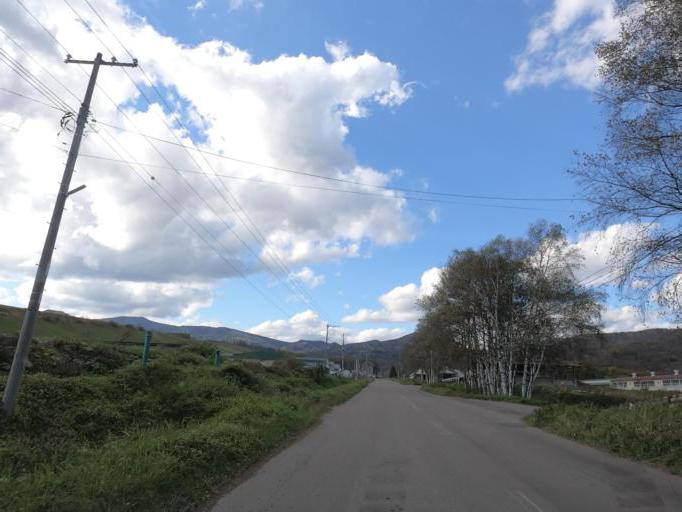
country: JP
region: Hokkaido
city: Otofuke
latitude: 43.2847
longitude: 143.2360
